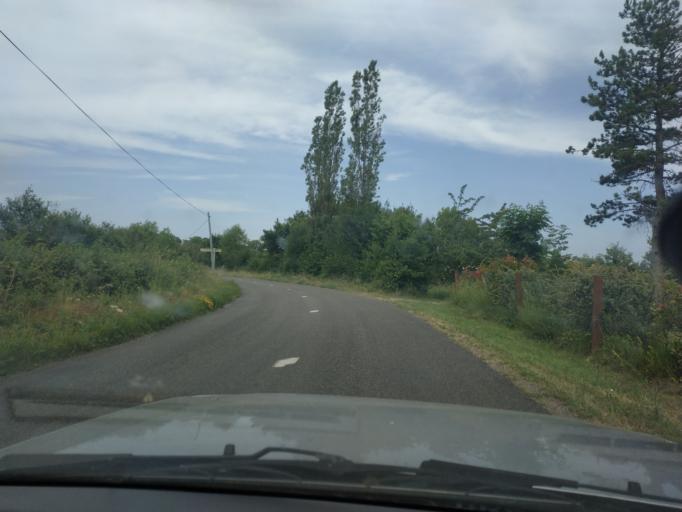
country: FR
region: Midi-Pyrenees
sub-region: Departement du Lot
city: Gramat
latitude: 44.6123
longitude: 1.6153
